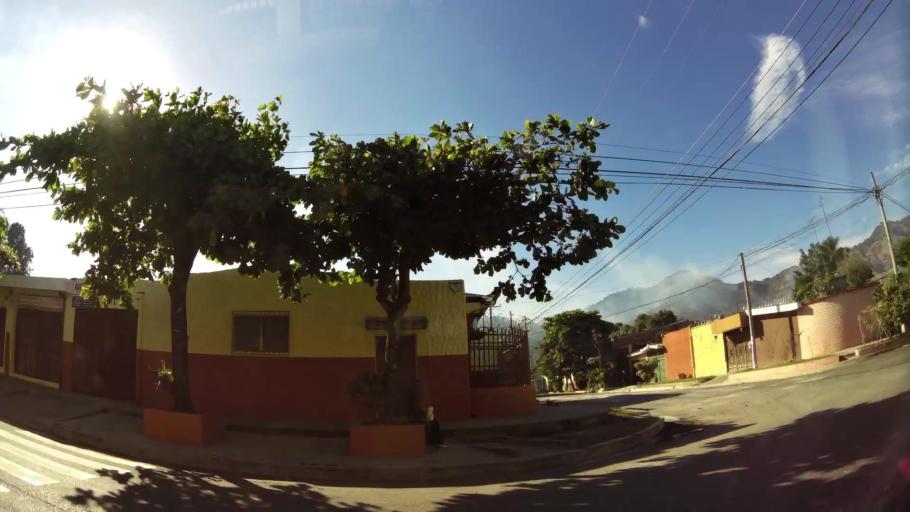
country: SV
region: Santa Ana
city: Santa Ana
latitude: 13.9994
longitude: -89.5631
